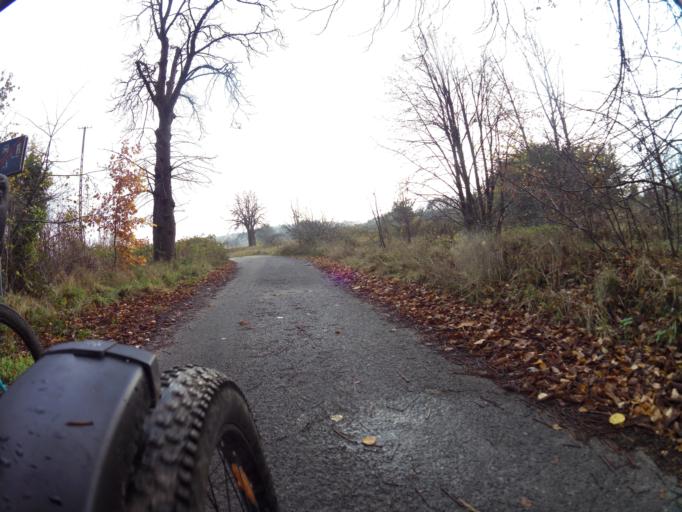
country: PL
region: Pomeranian Voivodeship
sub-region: Powiat wejherowski
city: Gniewino
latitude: 54.7106
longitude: 18.0979
